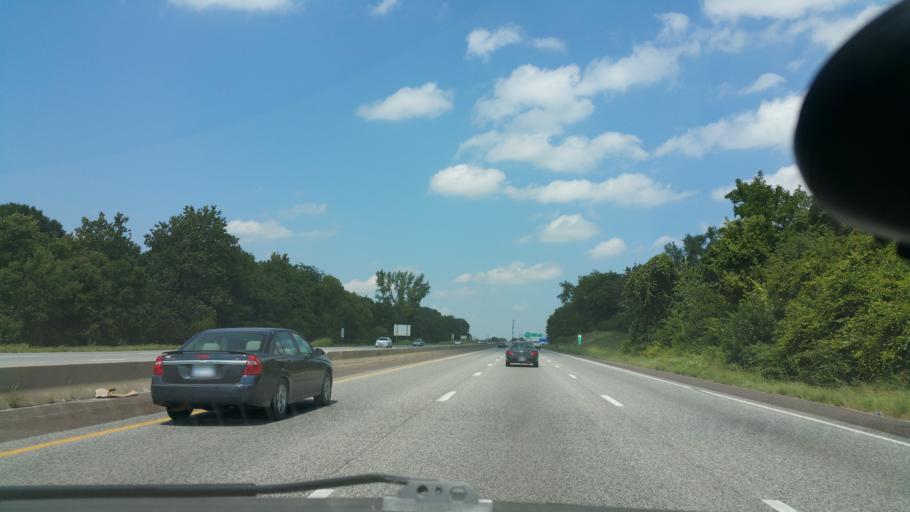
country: US
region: Missouri
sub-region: Clay County
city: North Kansas City
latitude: 39.1573
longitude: -94.5596
